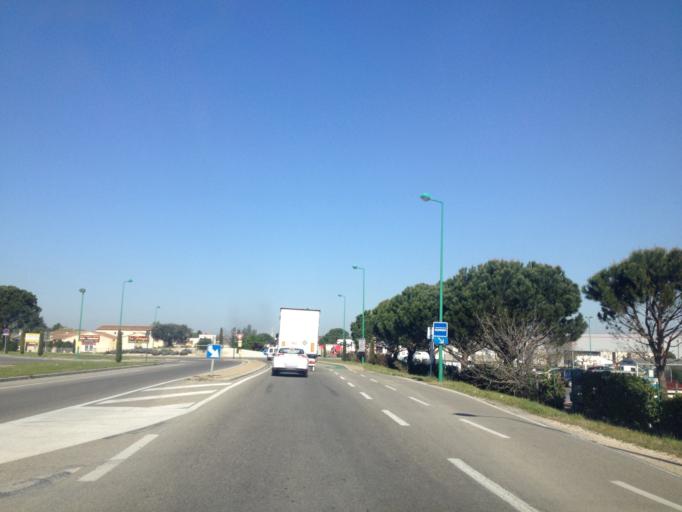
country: FR
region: Provence-Alpes-Cote d'Azur
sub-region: Departement du Vaucluse
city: Sarrians
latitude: 44.0805
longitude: 4.9830
